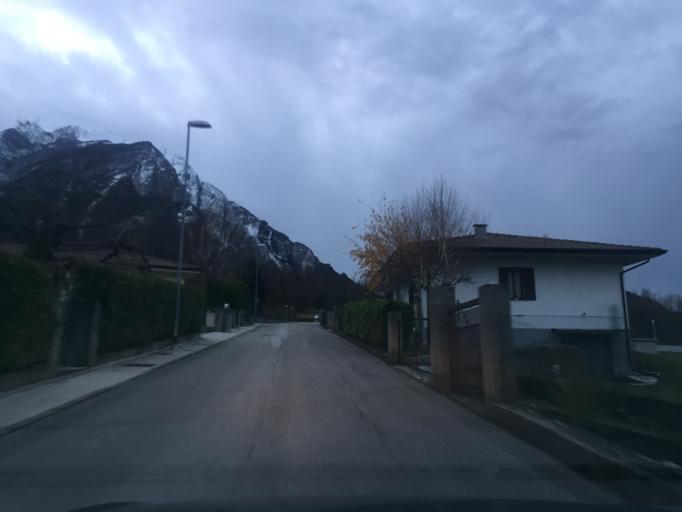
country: IT
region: Friuli Venezia Giulia
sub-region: Provincia di Udine
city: Venzone
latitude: 46.3229
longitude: 13.1385
